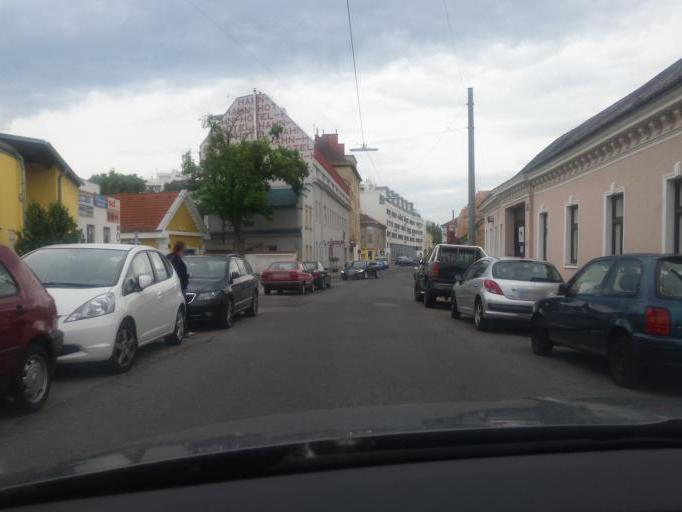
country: AT
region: Vienna
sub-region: Wien Stadt
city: Vienna
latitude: 48.1733
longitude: 16.4205
